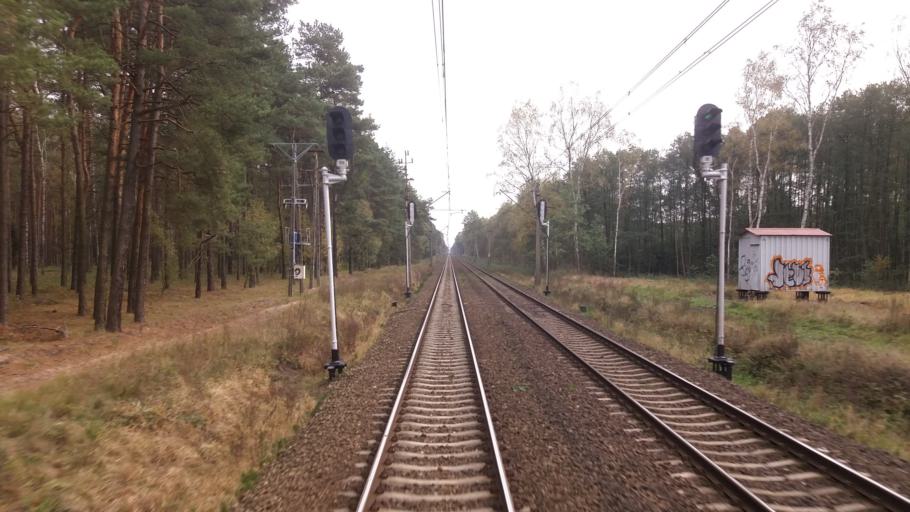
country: PL
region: West Pomeranian Voivodeship
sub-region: Powiat stargardzki
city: Kobylanka
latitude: 53.3791
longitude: 14.8027
